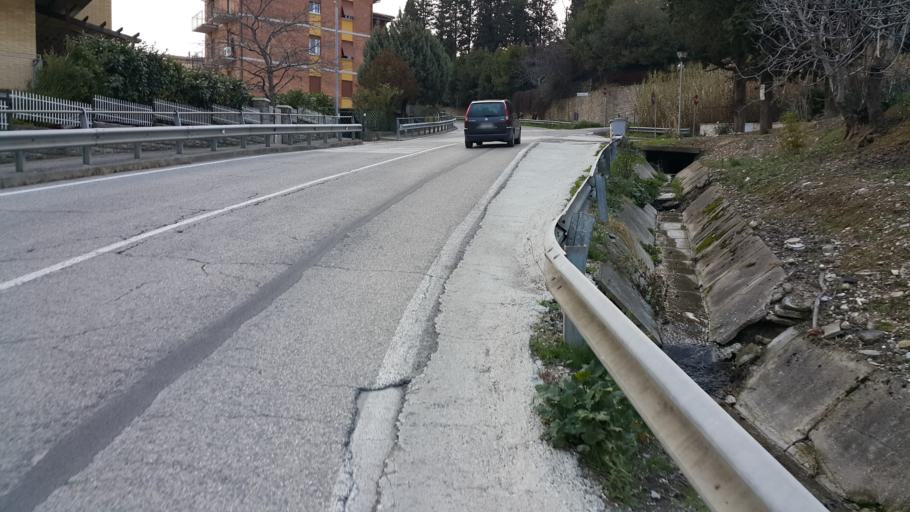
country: IT
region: Umbria
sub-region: Provincia di Perugia
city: Perugia
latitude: 43.0879
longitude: 12.3722
